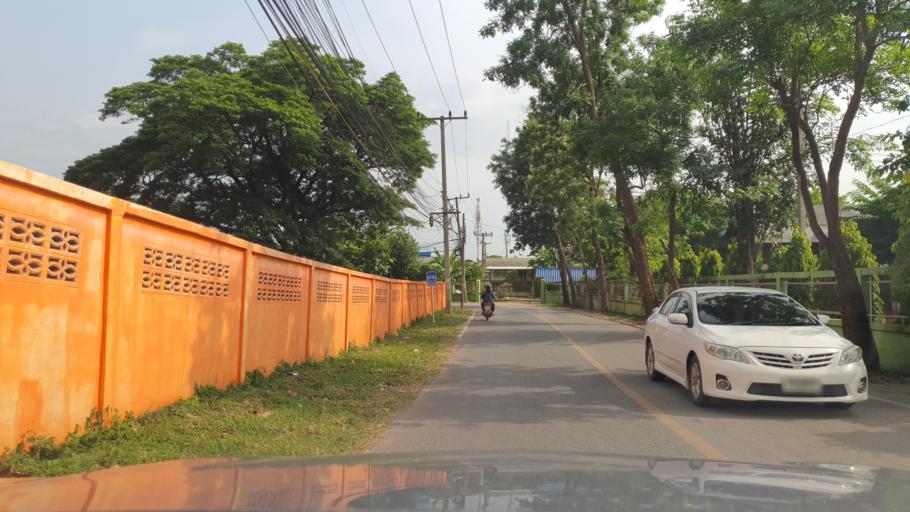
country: TH
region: Phitsanulok
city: Phitsanulok
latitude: 16.8427
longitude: 100.2604
